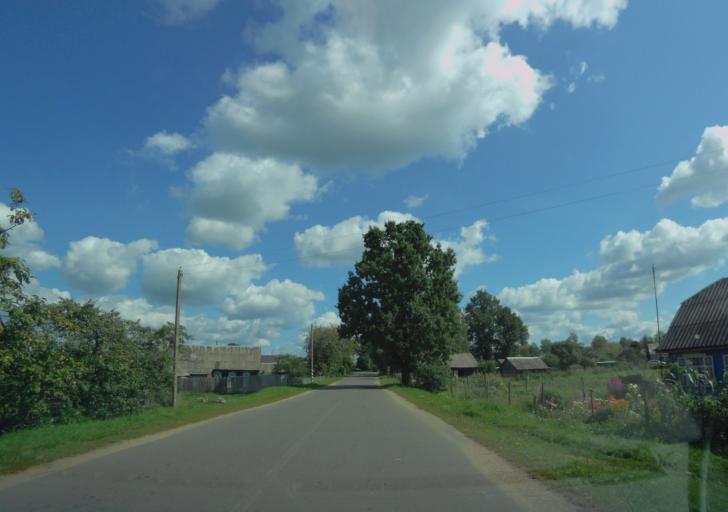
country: BY
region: Minsk
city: Horad Barysaw
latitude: 54.4276
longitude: 28.4282
